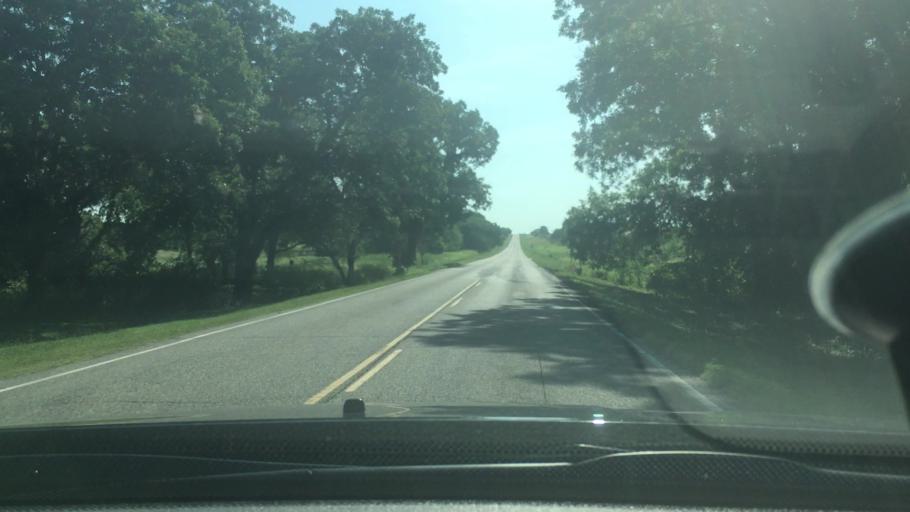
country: US
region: Oklahoma
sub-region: Garvin County
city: Pauls Valley
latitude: 34.6519
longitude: -97.2951
